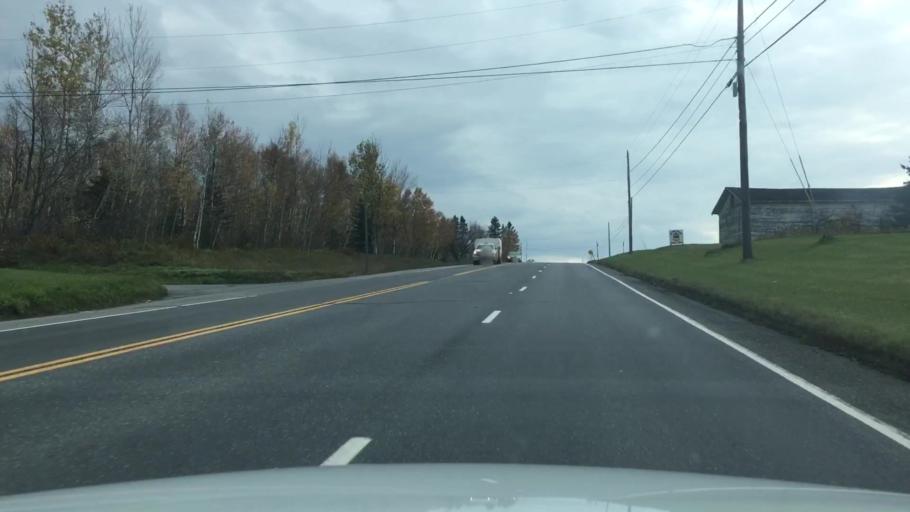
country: US
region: Maine
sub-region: Aroostook County
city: Caribou
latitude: 46.7818
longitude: -67.9891
